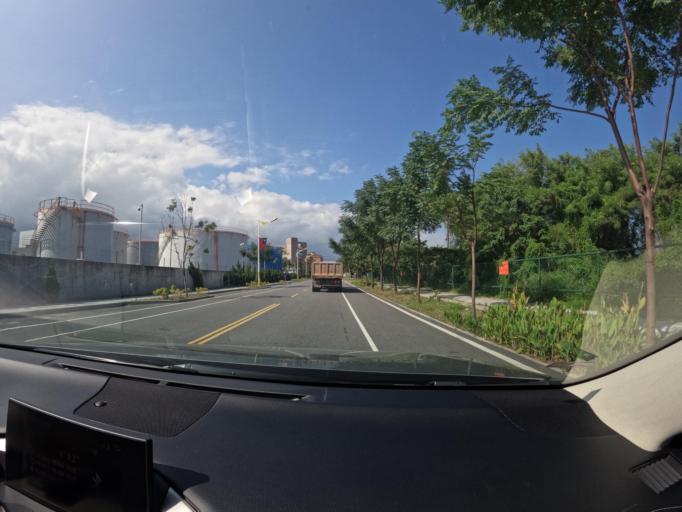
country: TW
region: Taiwan
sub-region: Hualien
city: Hualian
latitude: 23.9977
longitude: 121.6331
